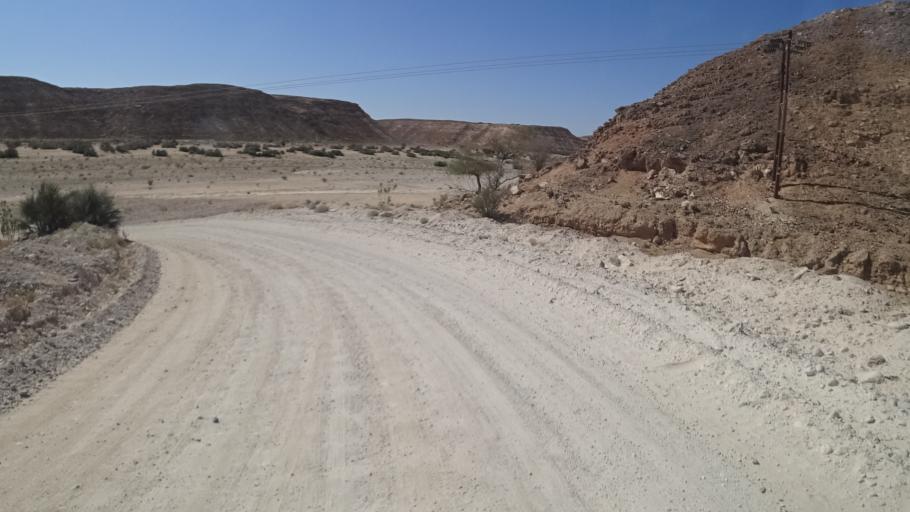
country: YE
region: Al Mahrah
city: Hawf
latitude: 17.3746
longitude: 53.1935
